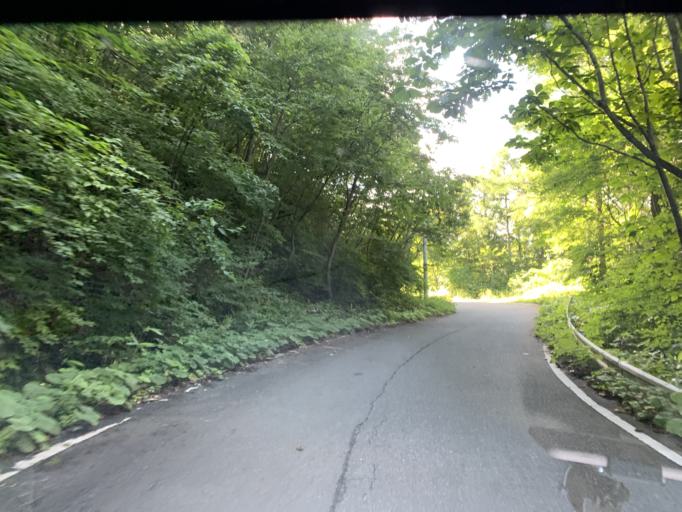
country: JP
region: Iwate
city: Ichinoseki
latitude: 38.9012
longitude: 140.8744
